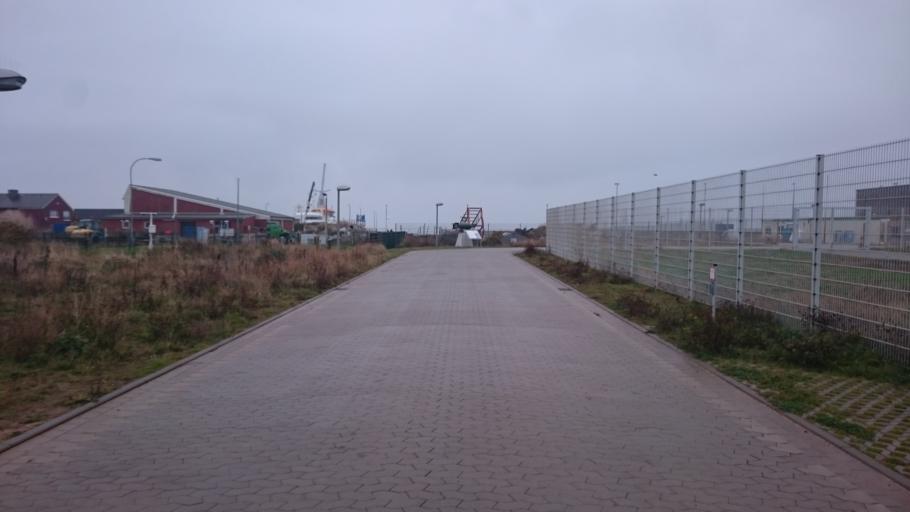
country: DE
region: Schleswig-Holstein
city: Helgoland
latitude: 54.1752
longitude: 7.8912
